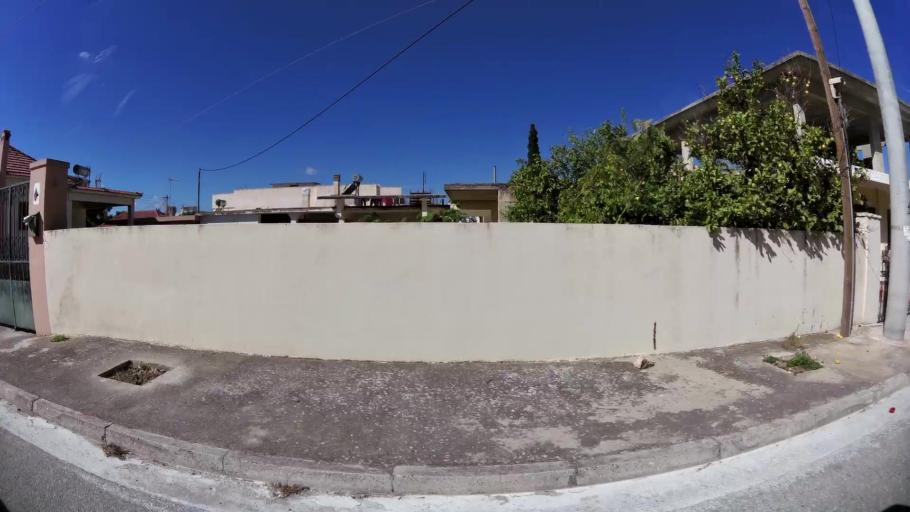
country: GR
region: Attica
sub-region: Nomarchia Anatolikis Attikis
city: Markopoulo
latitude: 37.8850
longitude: 23.9390
